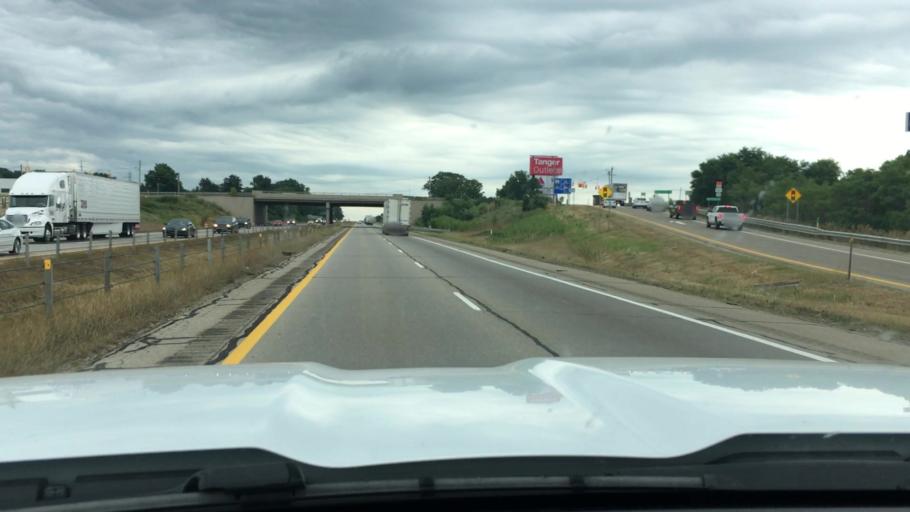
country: US
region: Michigan
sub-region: Kent County
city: Cutlerville
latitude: 42.8137
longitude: -85.6690
